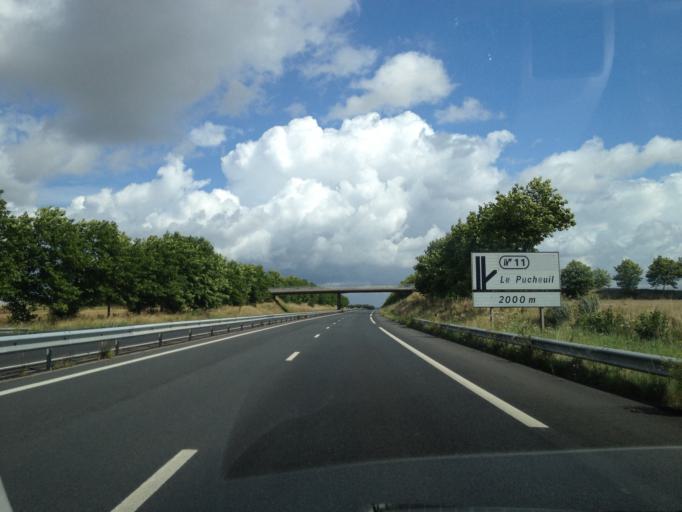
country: FR
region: Haute-Normandie
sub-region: Departement de la Seine-Maritime
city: Saint-Martin-Osmonville
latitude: 49.6273
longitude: 1.2627
